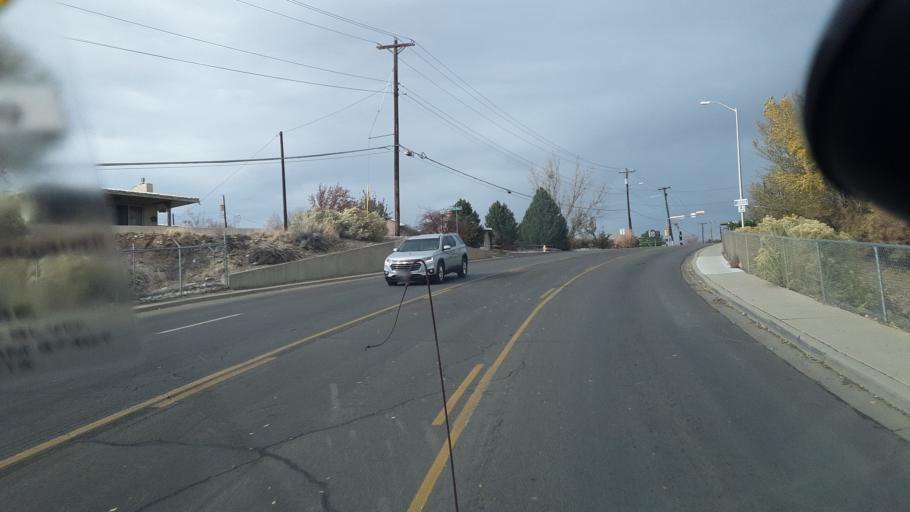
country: US
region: New Mexico
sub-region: San Juan County
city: Farmington
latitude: 36.7325
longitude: -108.1979
